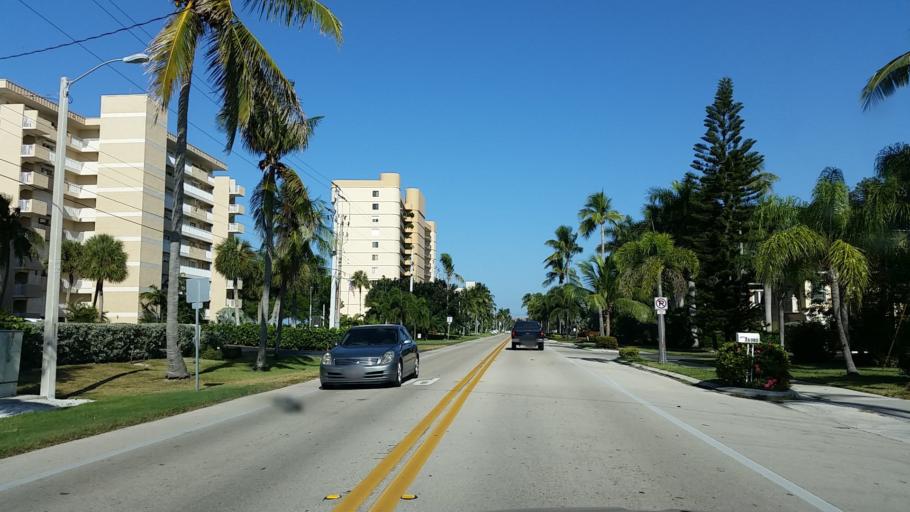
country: US
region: Florida
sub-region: Lee County
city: Bonita Springs
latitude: 26.3540
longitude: -81.8559
